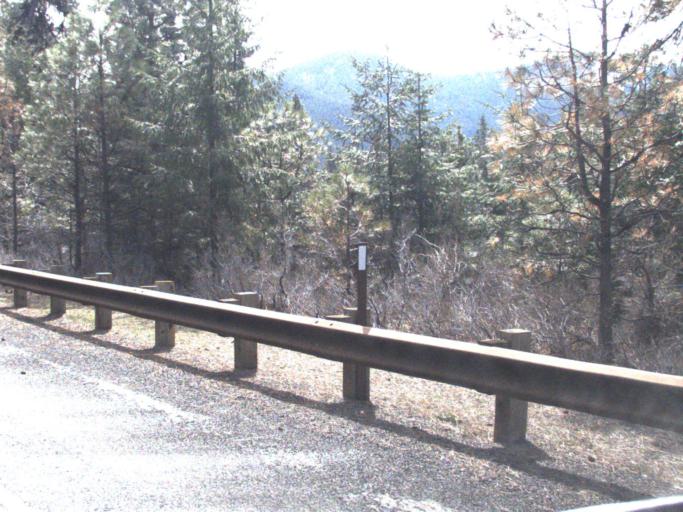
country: US
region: Washington
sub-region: Kittitas County
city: Cle Elum
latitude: 46.9279
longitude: -121.0469
